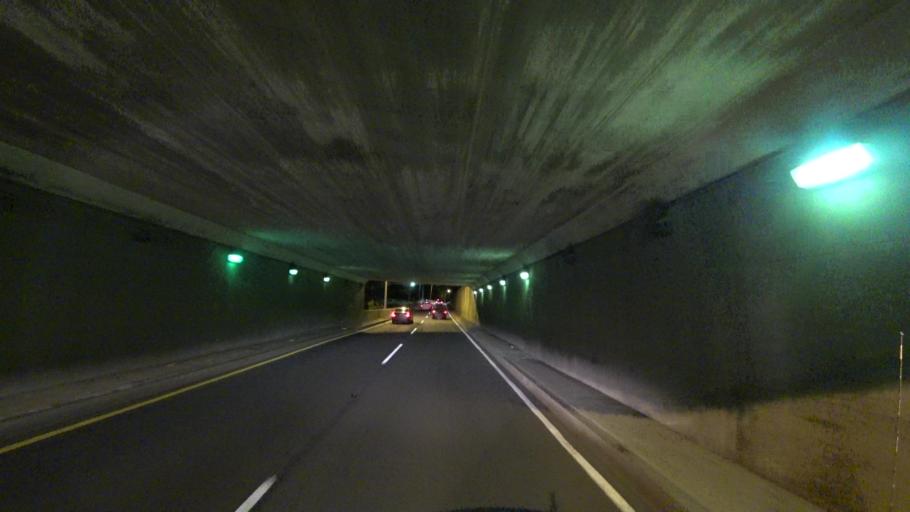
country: US
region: Massachusetts
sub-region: Middlesex County
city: Watertown
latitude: 42.3614
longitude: -71.1462
